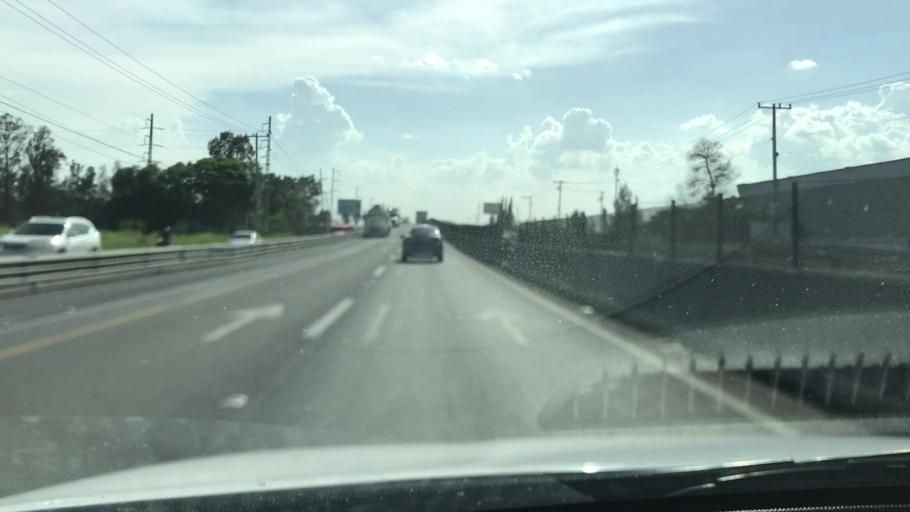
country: MX
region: Guanajuato
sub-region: Celaya
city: Colonia Fraccionamiento el Puente
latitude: 20.5155
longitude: -100.8907
